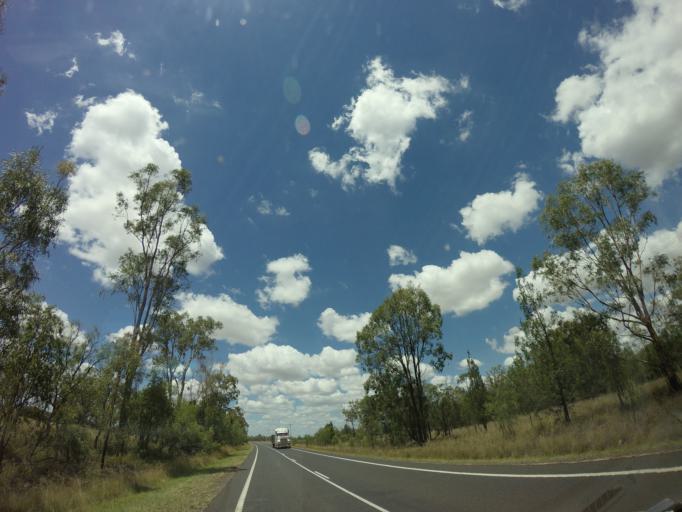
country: AU
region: Queensland
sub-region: Toowoomba
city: Oakey
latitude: -27.8867
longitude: 151.2203
